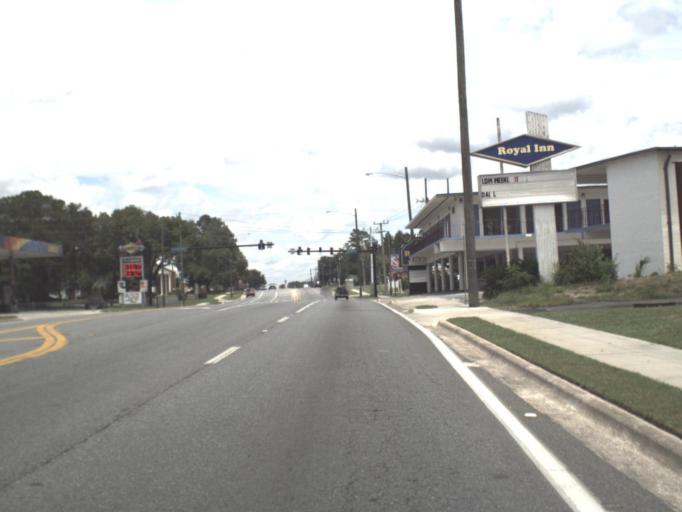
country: US
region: Florida
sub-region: Suwannee County
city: Live Oak
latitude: 30.3039
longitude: -82.9801
